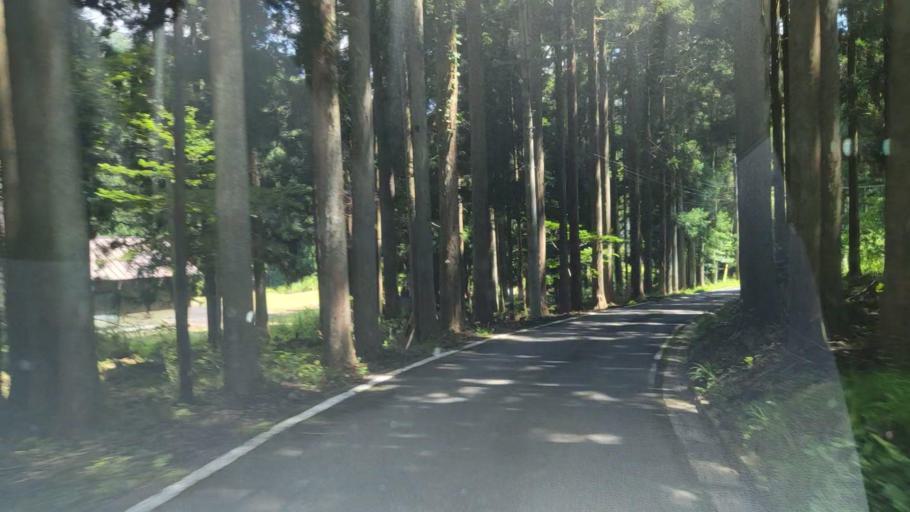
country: JP
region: Fukui
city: Ono
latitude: 35.7509
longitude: 136.5799
